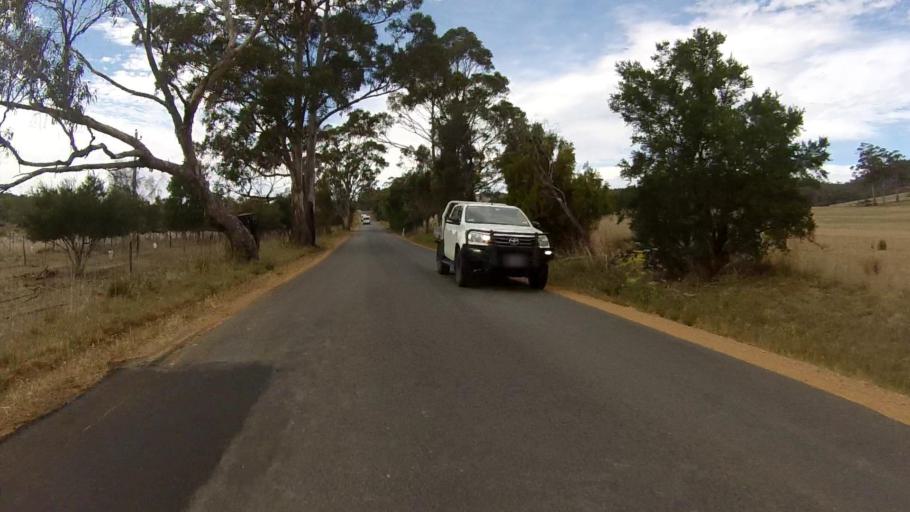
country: AU
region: Tasmania
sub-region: Clarence
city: Lindisfarne
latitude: -42.7455
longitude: 147.3696
